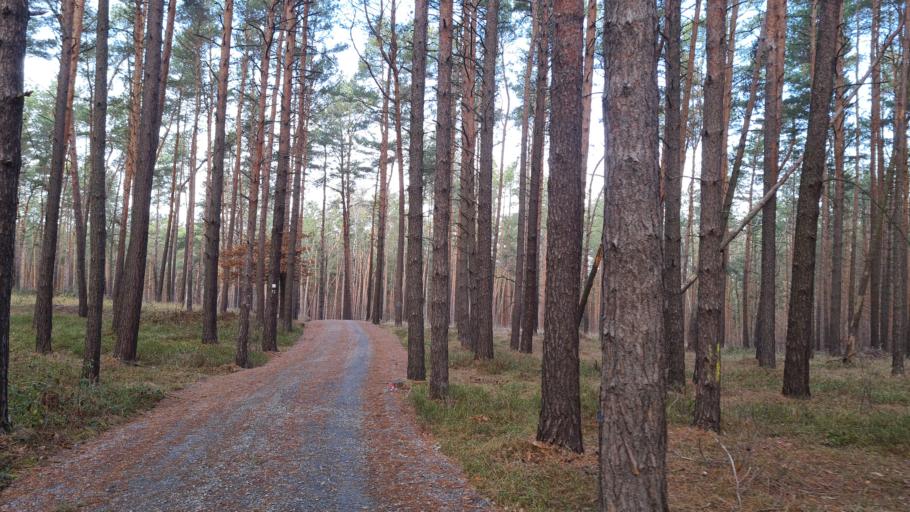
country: DE
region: Brandenburg
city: Groden
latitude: 51.3896
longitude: 13.5789
